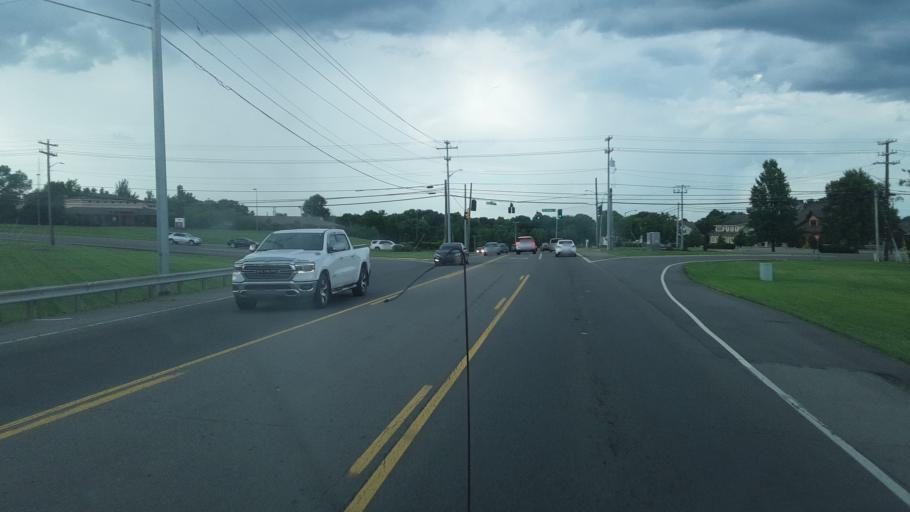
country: US
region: Tennessee
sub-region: Montgomery County
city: Clarksville
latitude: 36.5204
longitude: -87.2778
